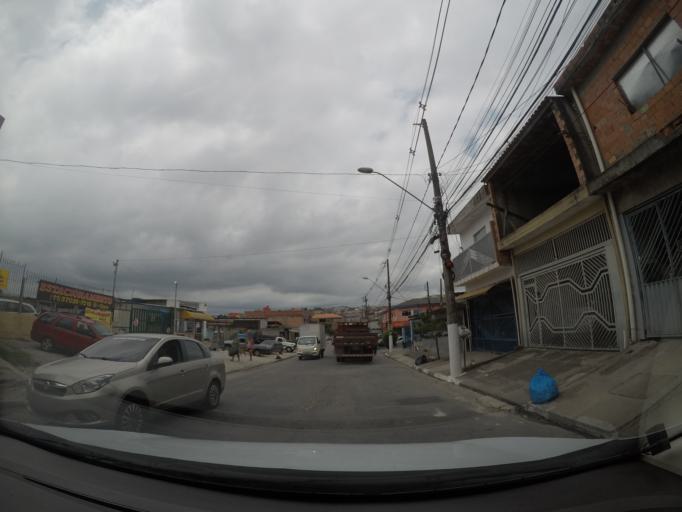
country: BR
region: Sao Paulo
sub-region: Itaquaquecetuba
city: Itaquaquecetuba
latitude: -23.4507
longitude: -46.4031
